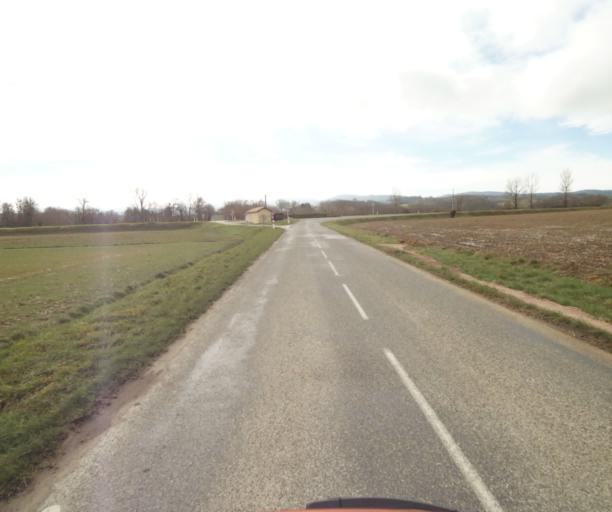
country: FR
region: Midi-Pyrenees
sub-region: Departement de l'Ariege
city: Pamiers
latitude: 43.1089
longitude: 1.5474
